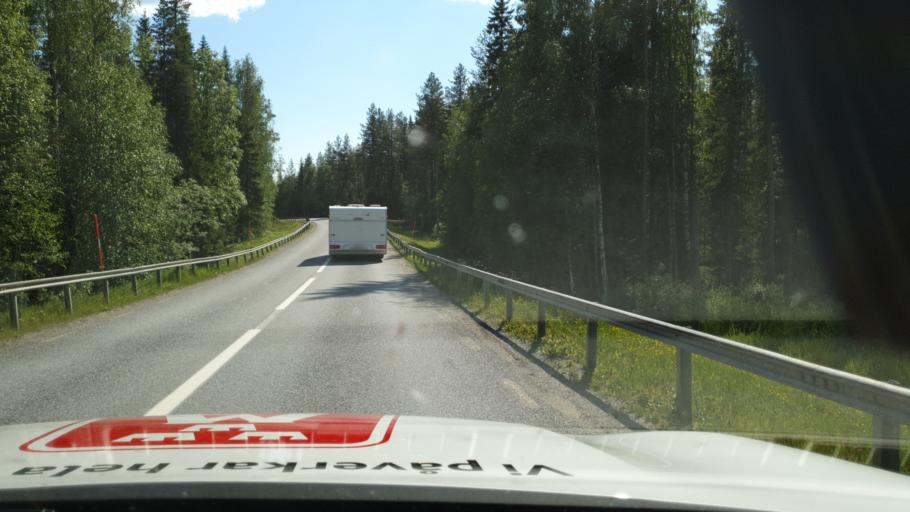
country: SE
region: Vaesterbotten
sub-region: Skelleftea Kommun
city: Burtraesk
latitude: 64.3470
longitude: 20.2344
